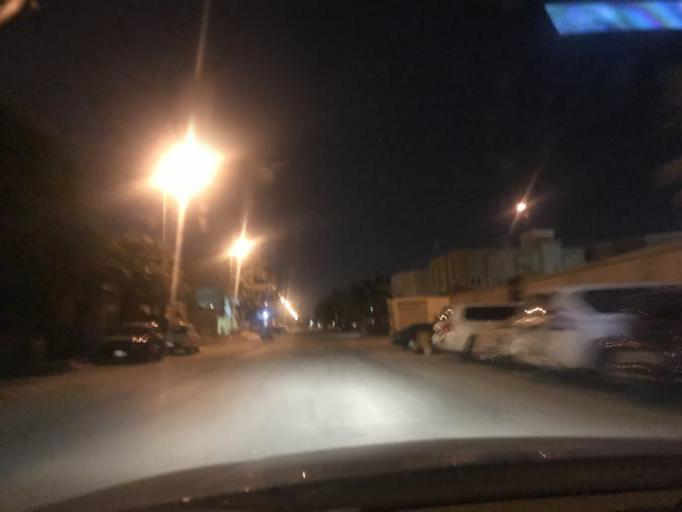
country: SA
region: Ar Riyad
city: Riyadh
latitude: 24.7415
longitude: 46.7821
